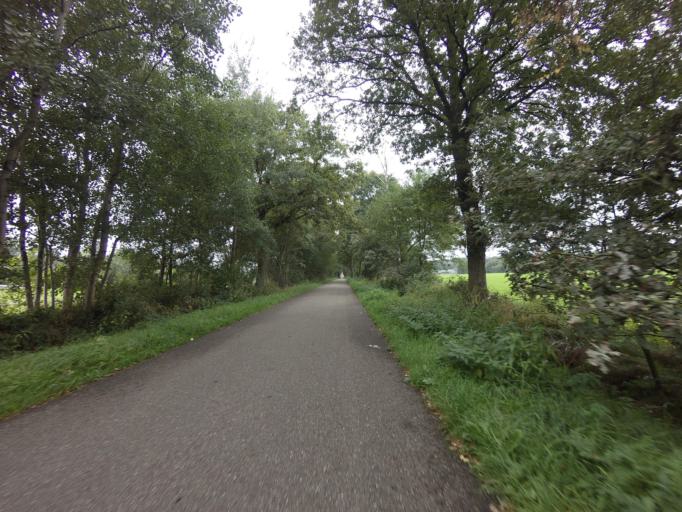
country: NL
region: Overijssel
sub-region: Gemeente Enschede
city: Enschede
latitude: 52.1915
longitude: 6.9268
